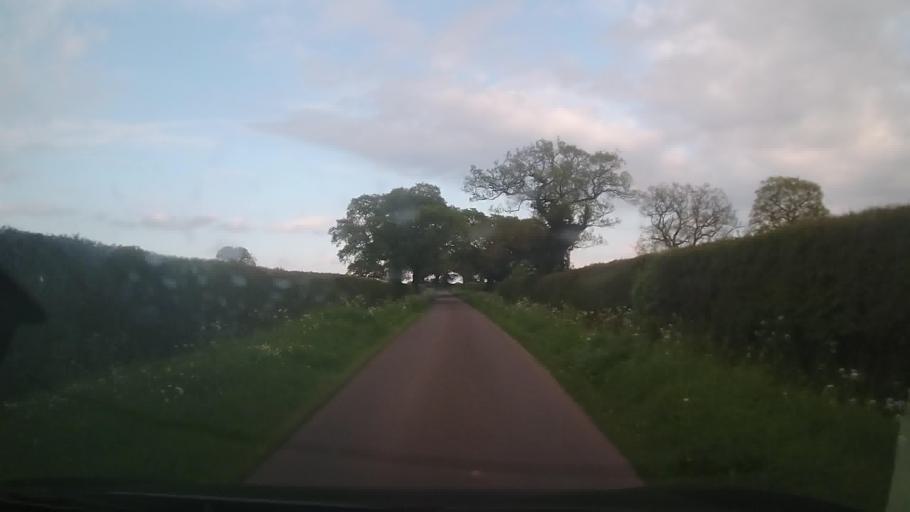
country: GB
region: England
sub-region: Shropshire
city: Ellesmere
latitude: 52.9342
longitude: -2.9032
